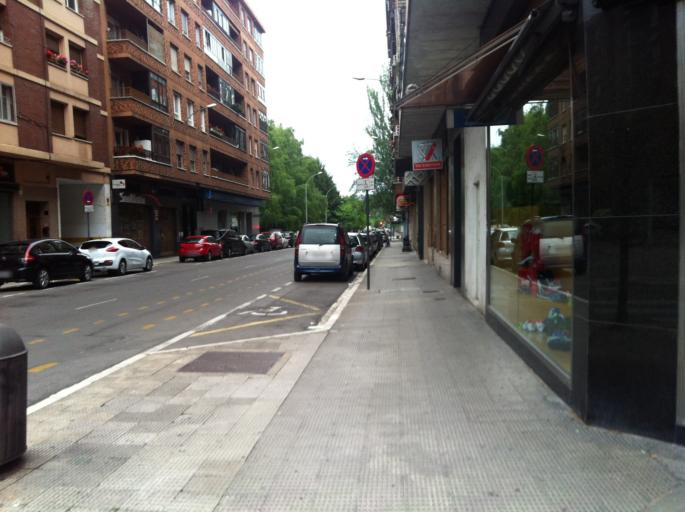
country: ES
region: Basque Country
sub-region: Provincia de Alava
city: Gasteiz / Vitoria
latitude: 42.8507
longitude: -2.6846
